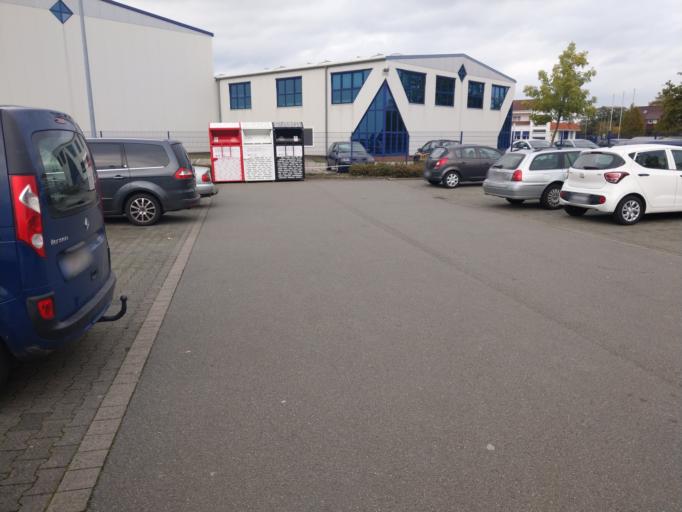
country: DE
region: Lower Saxony
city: Diepholz
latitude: 52.6151
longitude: 8.3652
